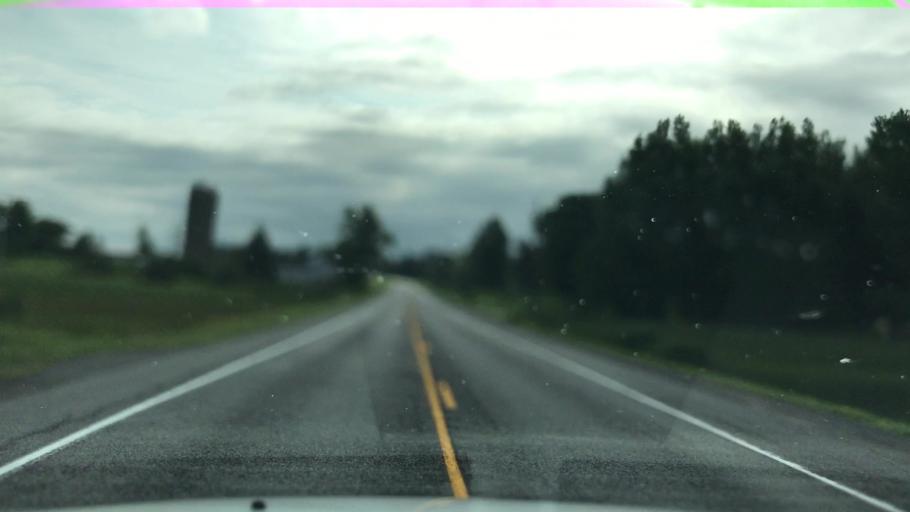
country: US
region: New York
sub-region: Erie County
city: Alden
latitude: 42.8354
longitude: -78.4124
